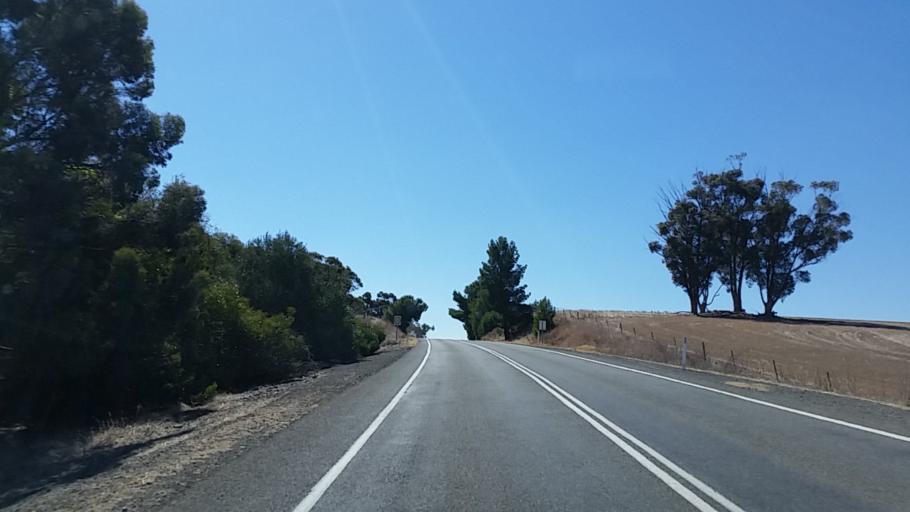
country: AU
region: South Australia
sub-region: Light
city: Kapunda
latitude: -34.0727
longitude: 138.7881
